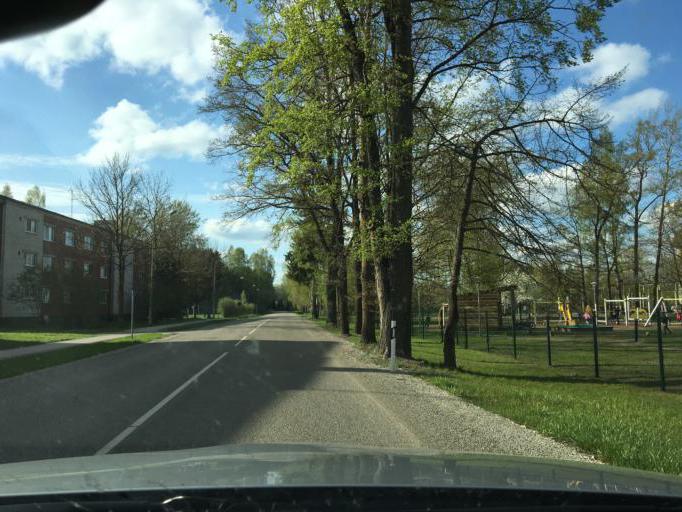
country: LV
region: Ozolnieku
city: Ozolnieki
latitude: 56.6832
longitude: 23.8354
